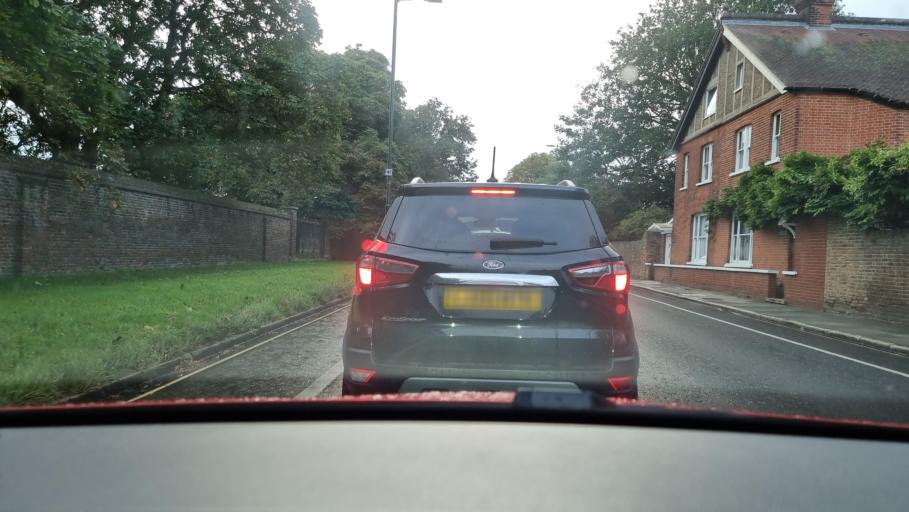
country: GB
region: England
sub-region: Greater London
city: Teddington
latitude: 51.4070
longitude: -0.3288
